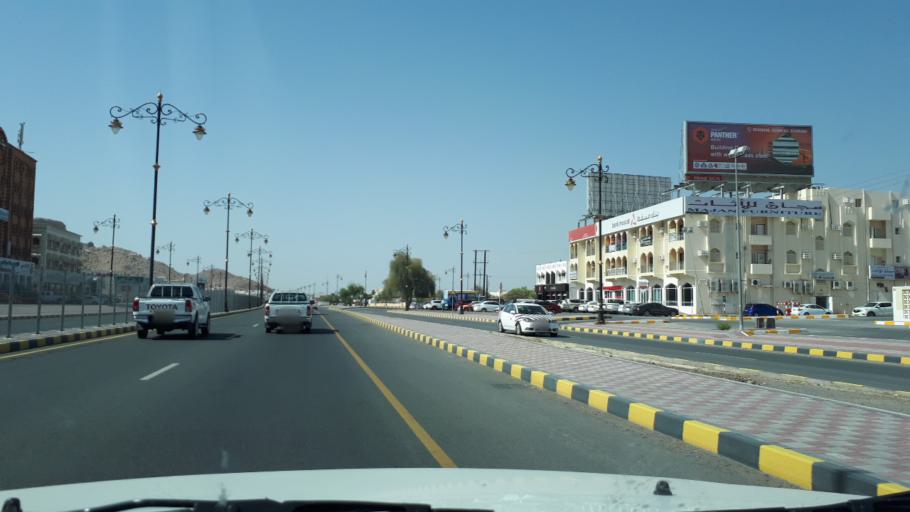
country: OM
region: Muhafazat ad Dakhiliyah
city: Nizwa
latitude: 22.9010
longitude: 57.5325
